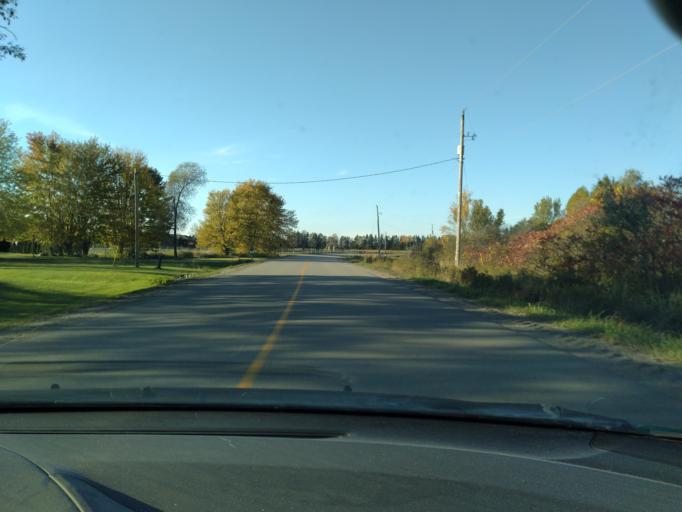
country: CA
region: Ontario
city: Bradford West Gwillimbury
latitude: 44.0197
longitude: -79.7266
